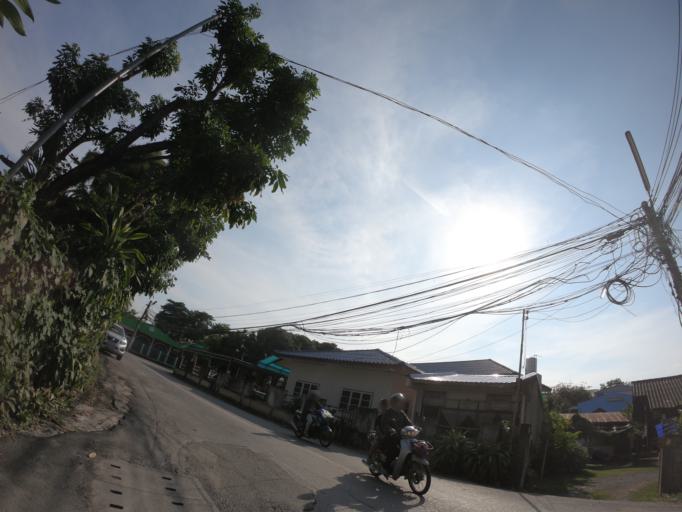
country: TH
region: Chiang Mai
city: Chiang Mai
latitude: 18.8217
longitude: 98.9935
